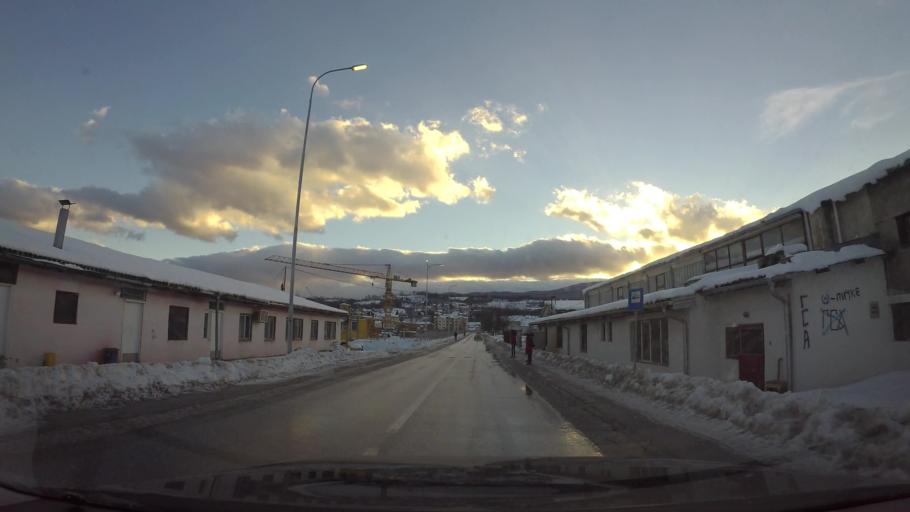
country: BA
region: Federation of Bosnia and Herzegovina
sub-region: Kanton Sarajevo
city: Sarajevo
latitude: 43.8139
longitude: 18.3647
